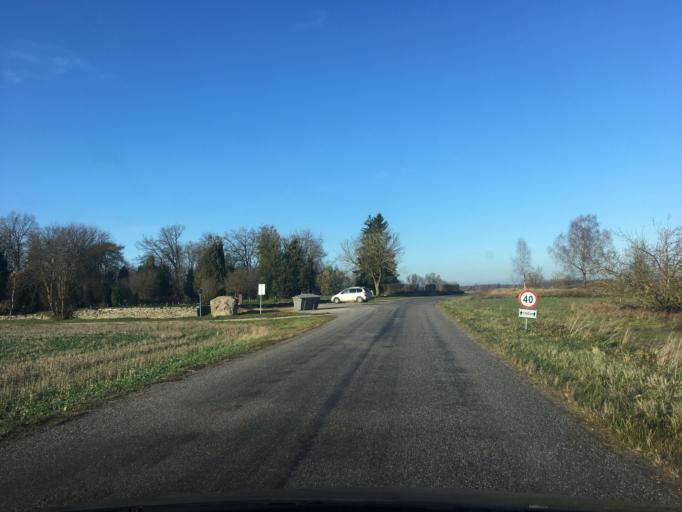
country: EE
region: Harju
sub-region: Raasiku vald
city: Arukula
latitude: 59.4488
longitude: 25.1181
